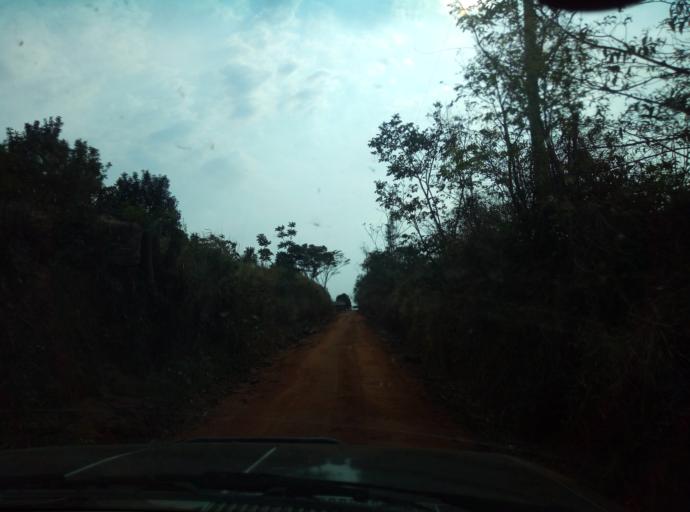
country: PY
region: Caaguazu
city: San Joaquin
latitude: -25.1477
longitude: -56.0992
